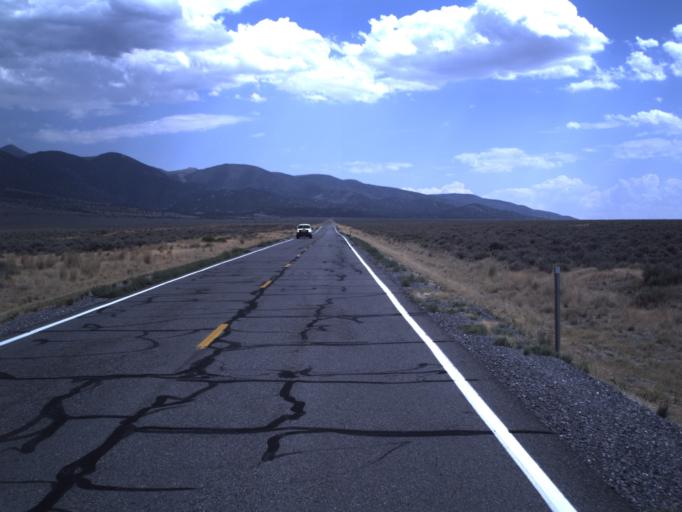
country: US
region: Utah
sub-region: Tooele County
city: Tooele
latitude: 40.3717
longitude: -112.3603
